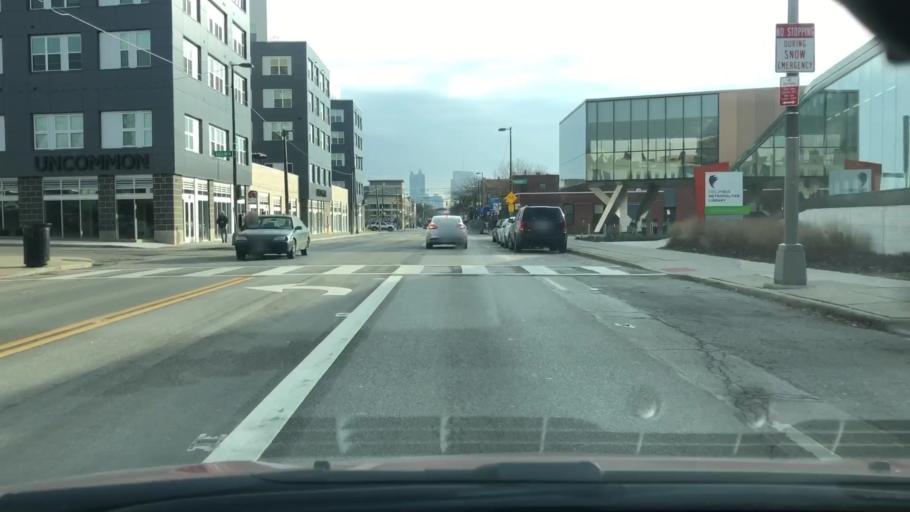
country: US
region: Ohio
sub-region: Franklin County
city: Columbus
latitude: 39.9914
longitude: -83.0064
